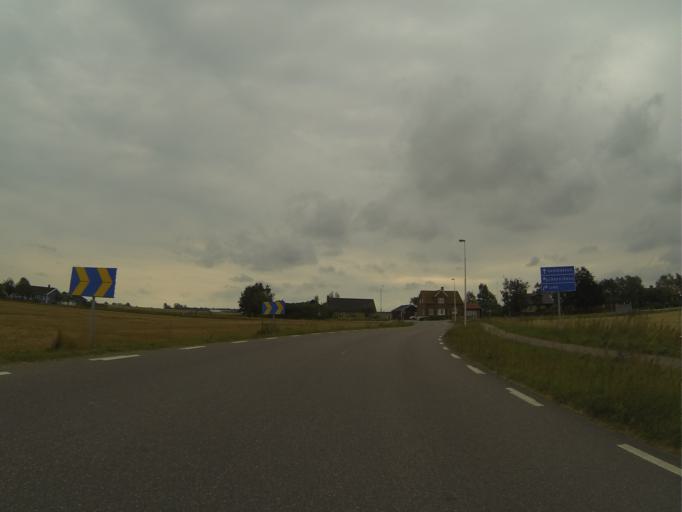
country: SE
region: Skane
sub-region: Lunds Kommun
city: Lund
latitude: 55.7414
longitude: 13.2776
